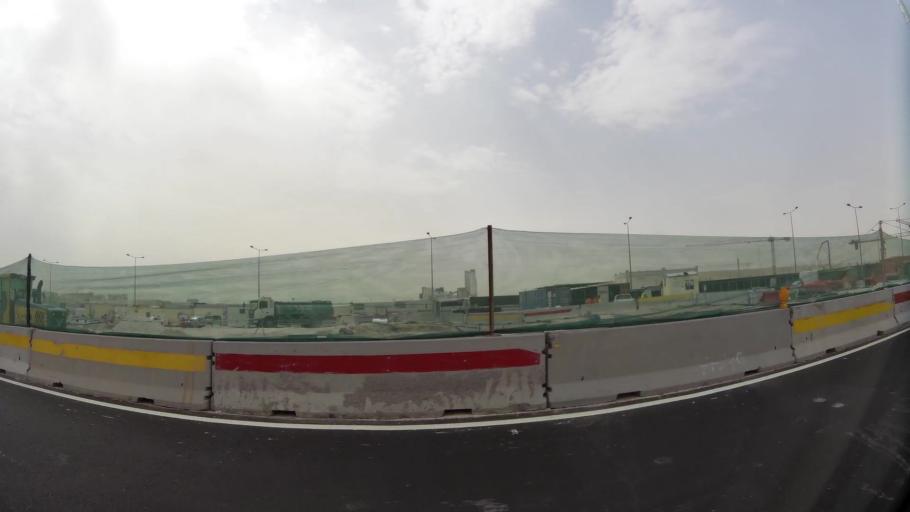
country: QA
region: Baladiyat ad Dawhah
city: Doha
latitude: 25.2936
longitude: 51.4878
